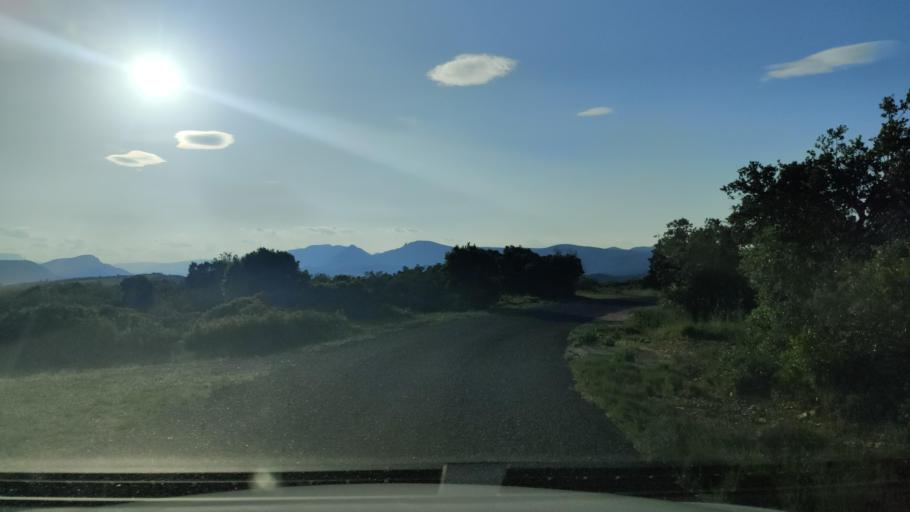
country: FR
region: Languedoc-Roussillon
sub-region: Departement des Pyrenees-Orientales
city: Estagel
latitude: 42.7932
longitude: 2.7273
